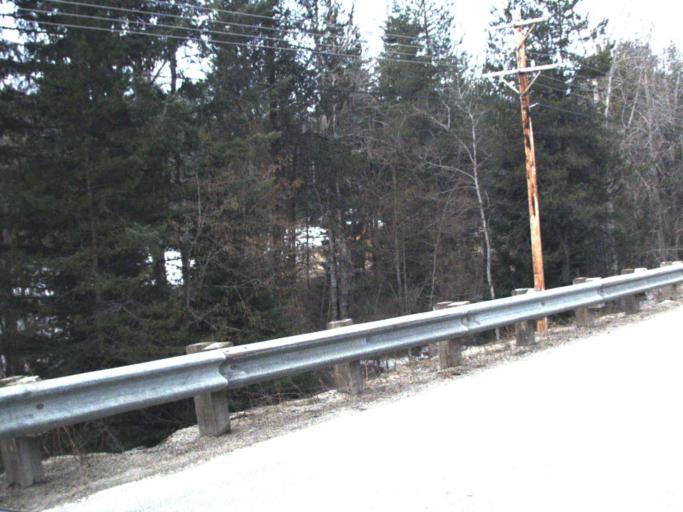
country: US
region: Washington
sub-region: Pend Oreille County
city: Newport
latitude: 48.2207
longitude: -117.1042
